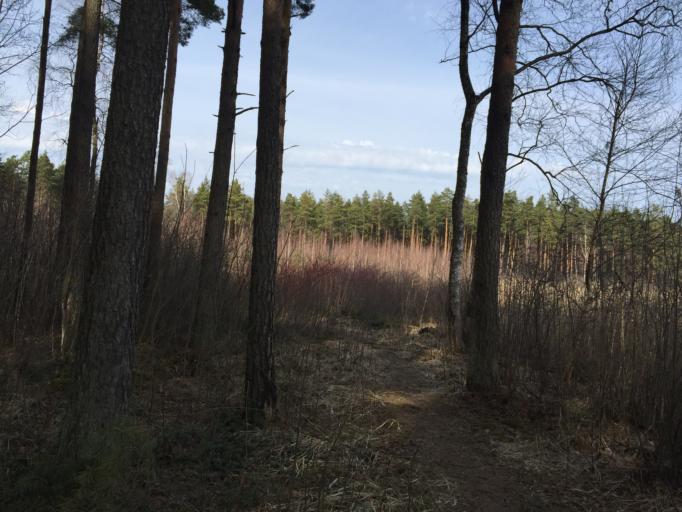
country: LV
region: Kekava
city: Balozi
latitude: 56.8739
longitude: 24.1310
